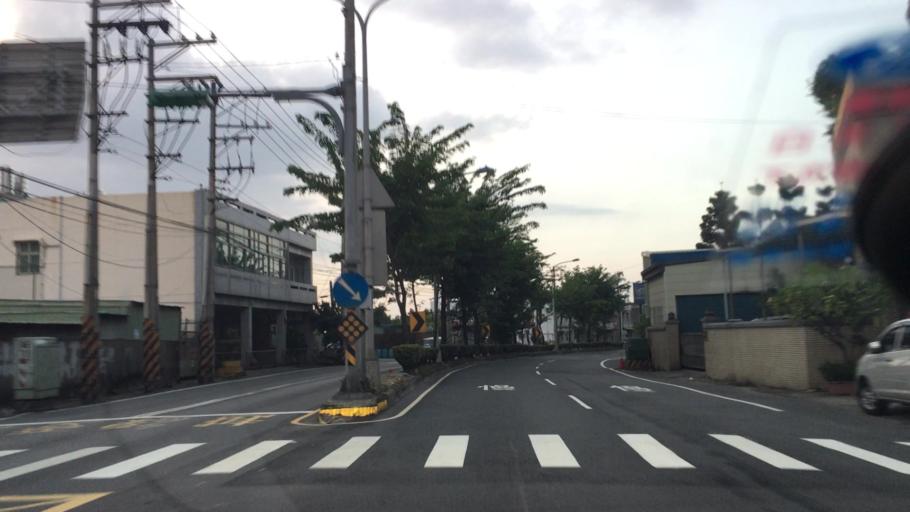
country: TW
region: Taiwan
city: Taoyuan City
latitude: 25.0570
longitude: 121.2685
